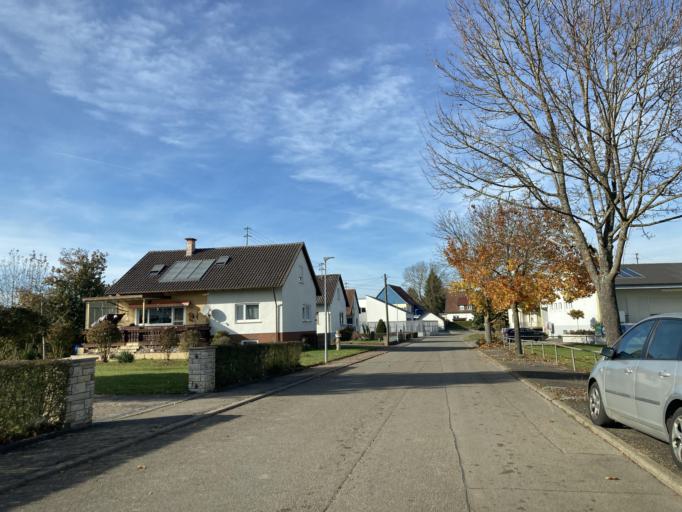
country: DE
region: Baden-Wuerttemberg
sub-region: Tuebingen Region
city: Hirrlingen
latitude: 48.4140
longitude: 8.9201
